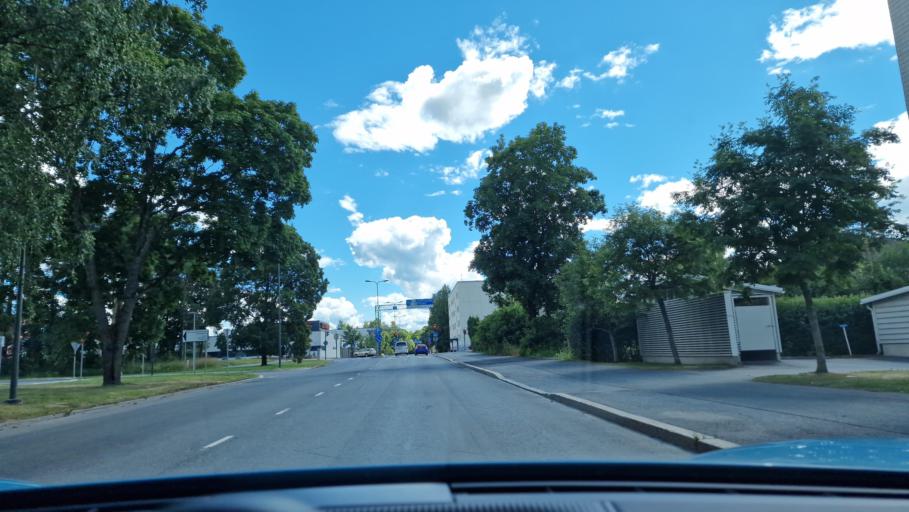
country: FI
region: Pirkanmaa
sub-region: Etelae-Pirkanmaa
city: Valkeakoski
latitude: 61.2695
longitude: 24.0297
